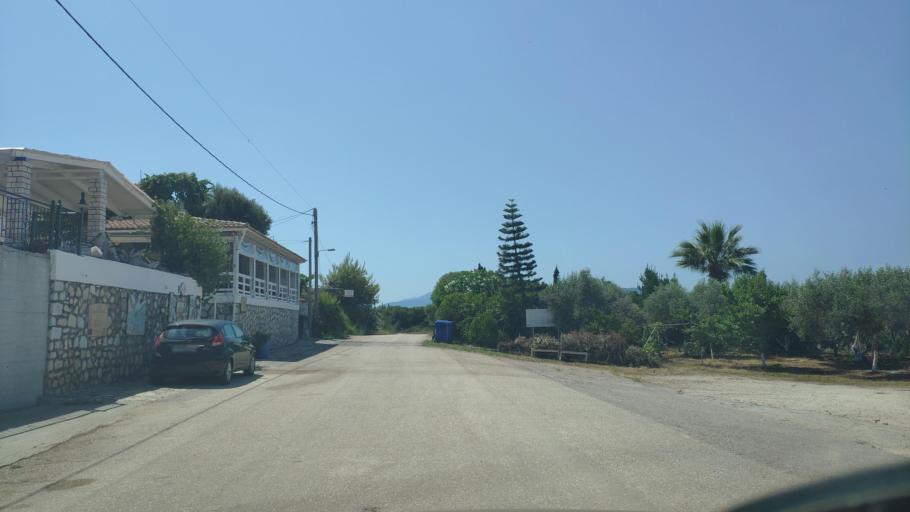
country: GR
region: Epirus
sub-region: Nomos Artas
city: Aneza
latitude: 39.0122
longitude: 20.9188
